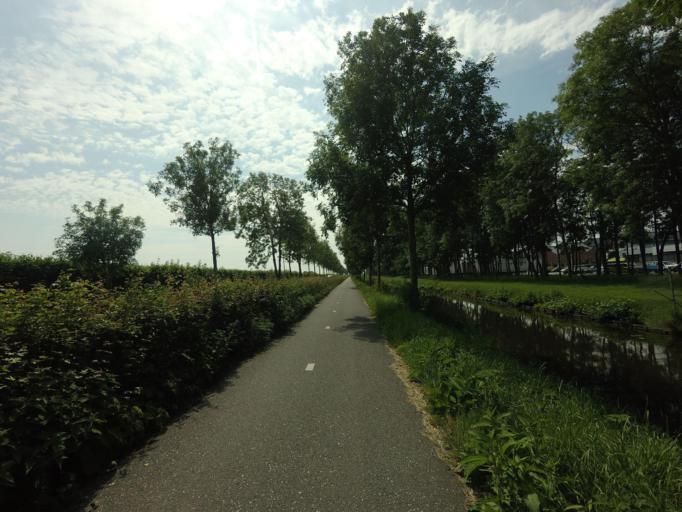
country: NL
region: North Holland
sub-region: Gemeente Medemblik
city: Medemblik
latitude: 52.7089
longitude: 5.1553
